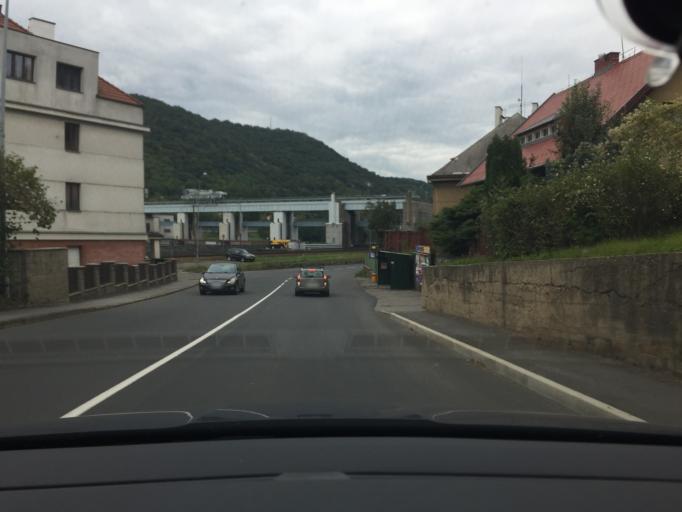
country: CZ
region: Ustecky
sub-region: Okres Usti nad Labem
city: Usti nad Labem
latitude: 50.6371
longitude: 14.0512
